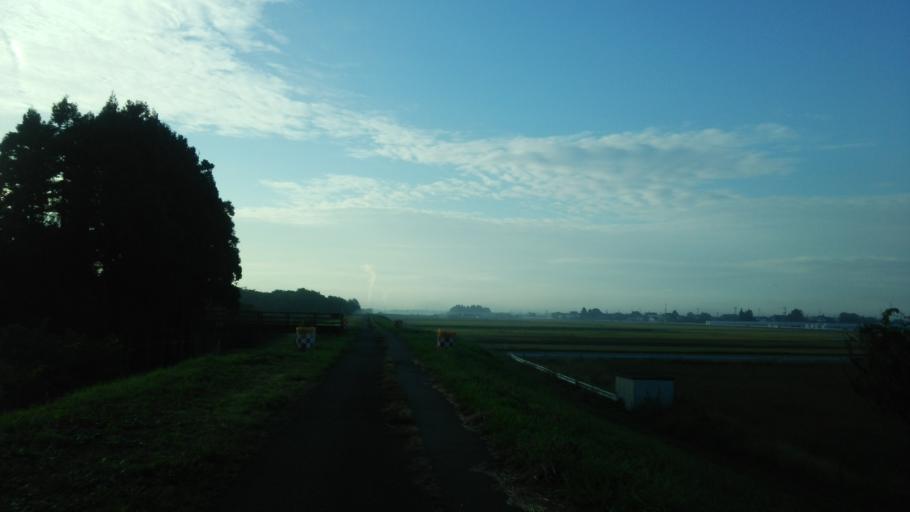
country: JP
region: Fukushima
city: Kitakata
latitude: 37.5475
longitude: 139.8599
